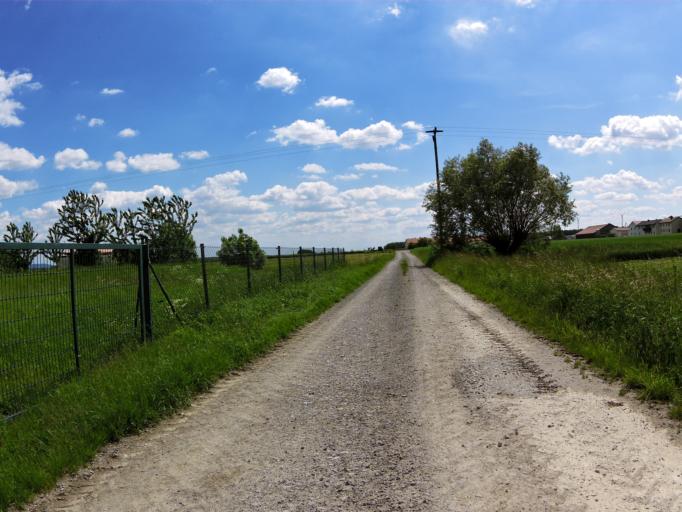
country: DE
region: Bavaria
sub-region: Regierungsbezirk Unterfranken
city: Biebelried
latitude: 49.7453
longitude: 10.0706
